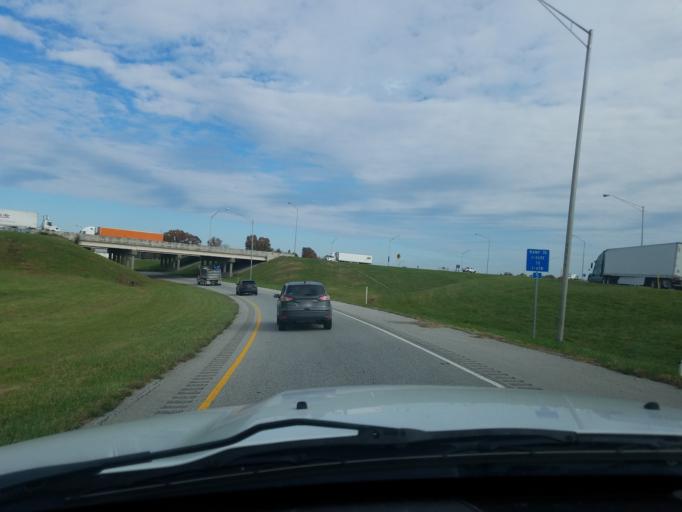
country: US
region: Indiana
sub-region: Clark County
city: Clarksville
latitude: 38.3446
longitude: -85.7521
